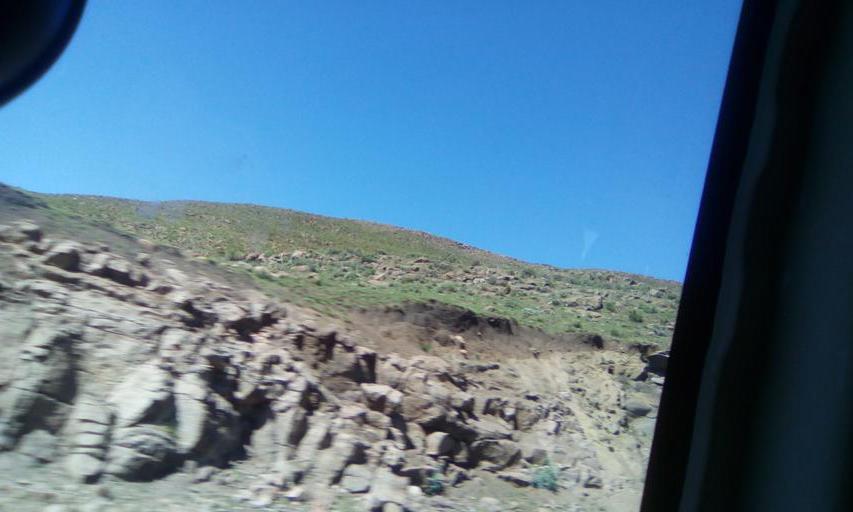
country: LS
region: Maseru
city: Nako
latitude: -29.8856
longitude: 28.0833
